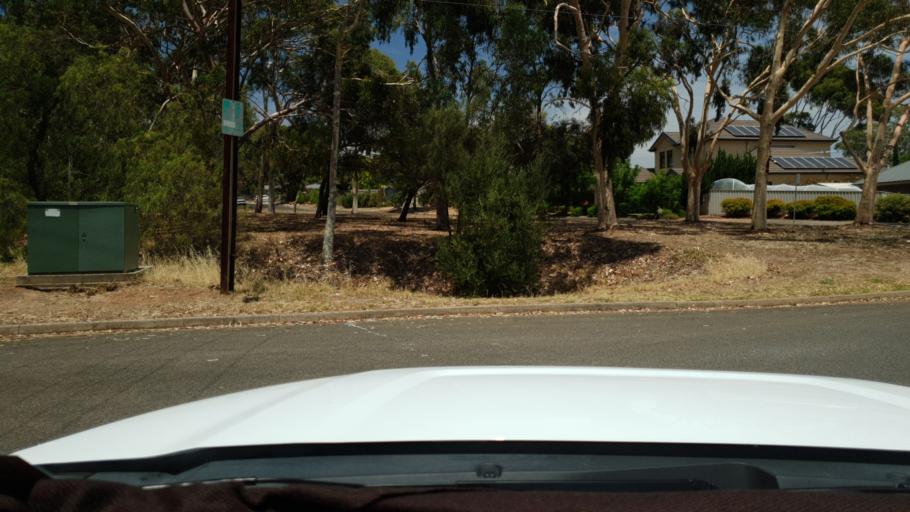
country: AU
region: South Australia
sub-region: Marion
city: Clovelly Park
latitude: -35.0071
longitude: 138.5856
